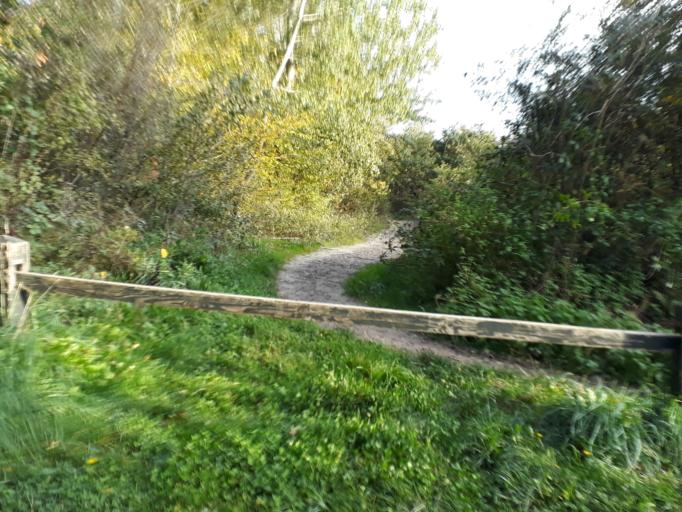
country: FR
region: Ile-de-France
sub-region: Departement de Seine-et-Marne
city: Bois-le-Roi
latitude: 48.4636
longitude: 2.7092
